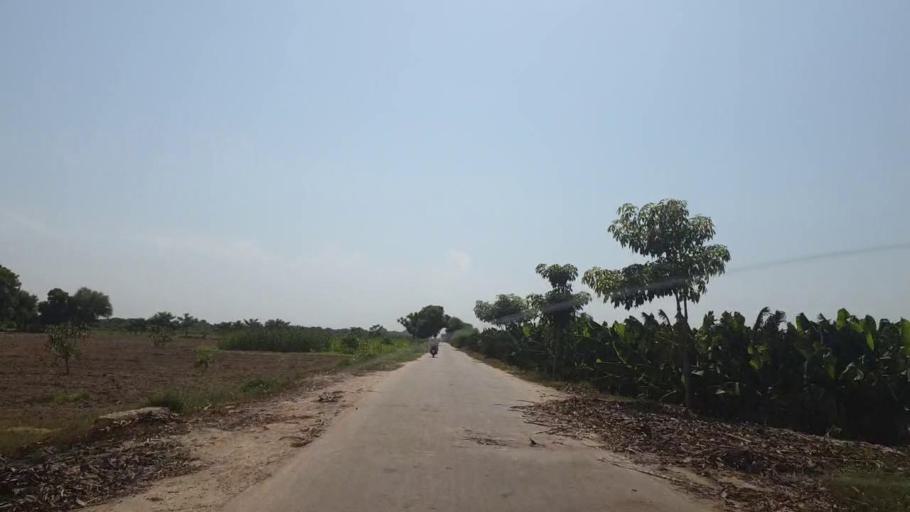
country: PK
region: Sindh
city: Tando Allahyar
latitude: 25.4021
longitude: 68.6439
